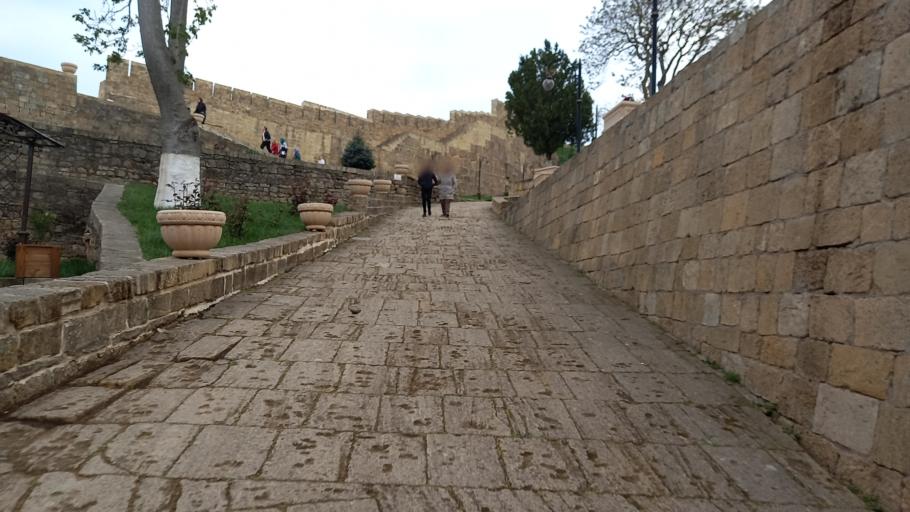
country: RU
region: Dagestan
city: Derbent
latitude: 42.0530
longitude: 48.2751
